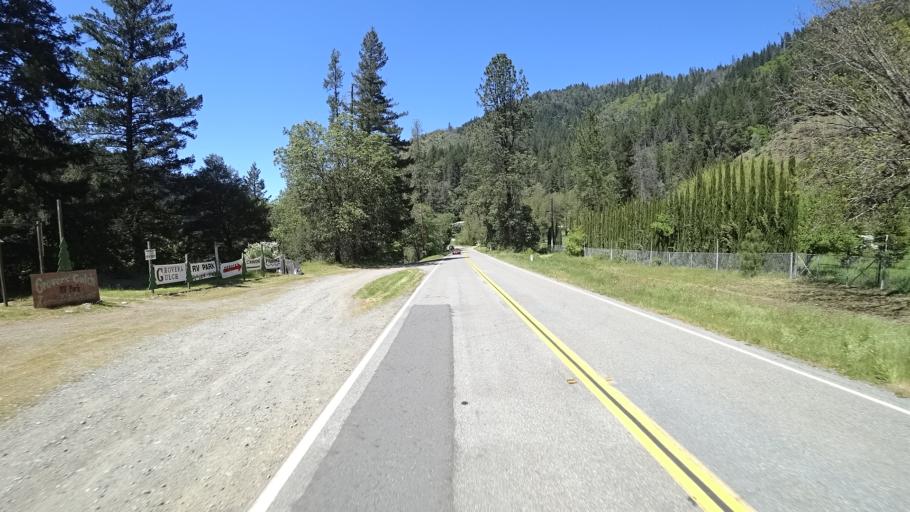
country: US
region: California
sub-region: Trinity County
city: Hayfork
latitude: 40.7456
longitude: -123.2691
